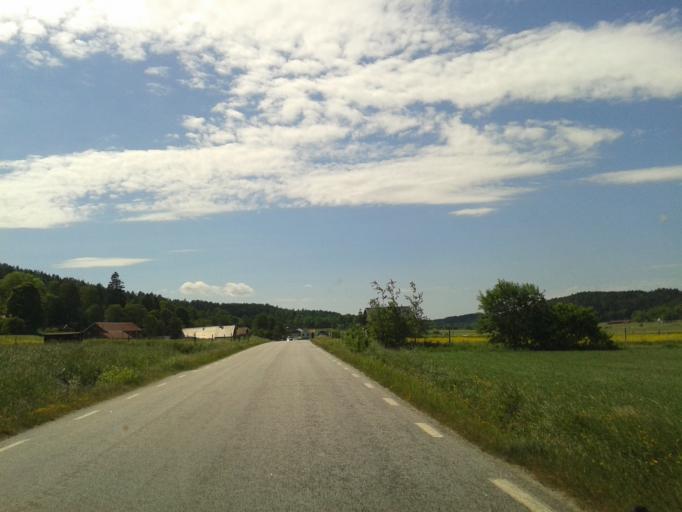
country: SE
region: Vaestra Goetaland
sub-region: Uddevalla Kommun
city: Uddevalla
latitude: 58.2892
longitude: 11.9336
